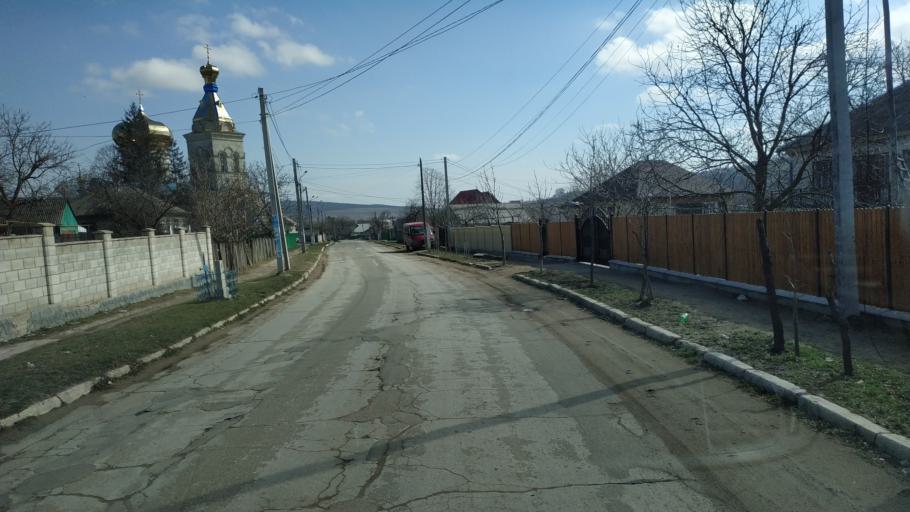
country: MD
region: Hincesti
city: Hincesti
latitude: 46.9727
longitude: 28.5792
